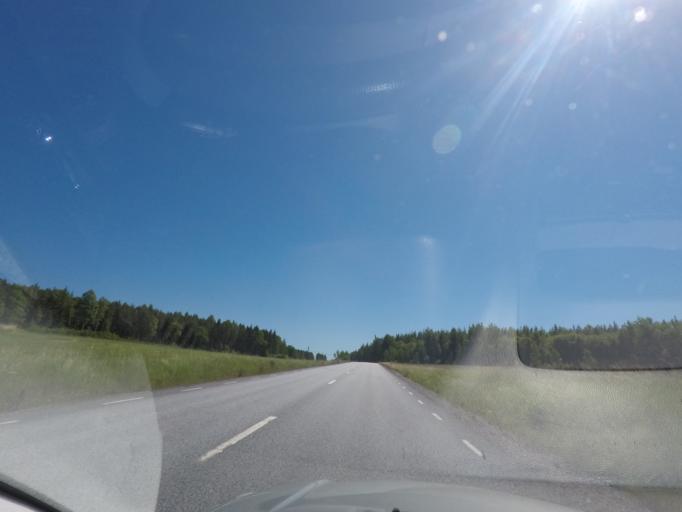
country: SE
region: Uppsala
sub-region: Habo Kommun
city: Balsta
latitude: 59.6460
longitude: 17.5661
